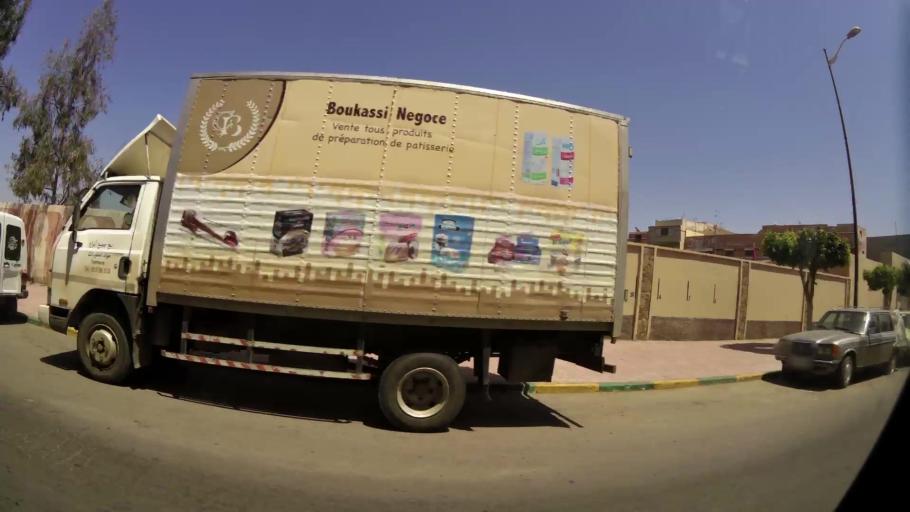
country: MA
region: Souss-Massa-Draa
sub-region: Inezgane-Ait Mellou
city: Inezgane
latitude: 30.3474
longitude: -9.5004
